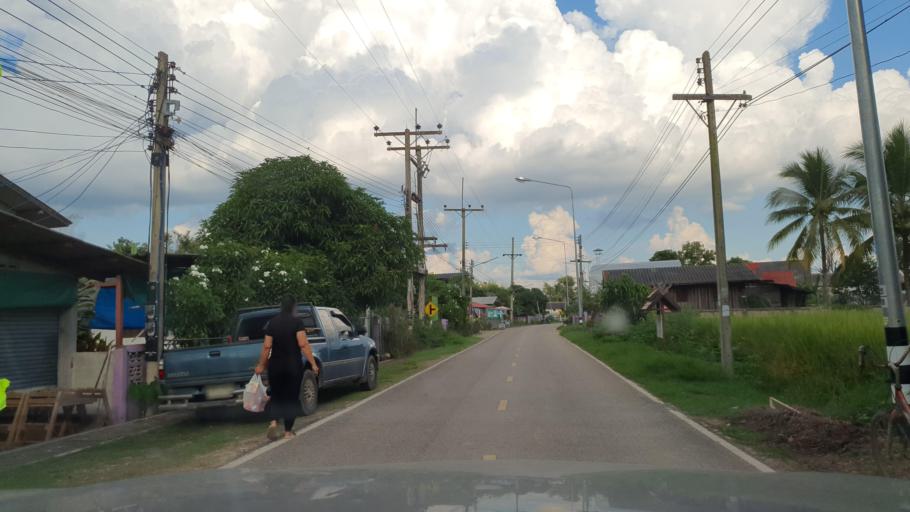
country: TH
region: Phayao
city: Phayao
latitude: 19.1799
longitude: 99.8423
